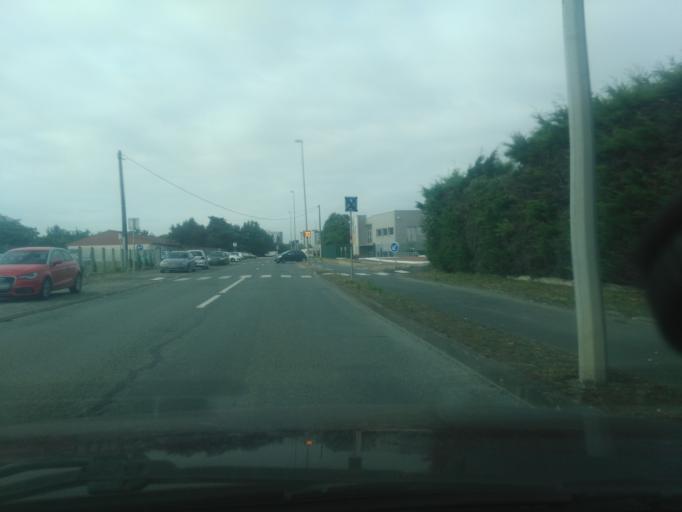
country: FR
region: Pays de la Loire
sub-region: Departement de la Vendee
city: La Roche-sur-Yon
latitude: 46.6860
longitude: -1.4334
